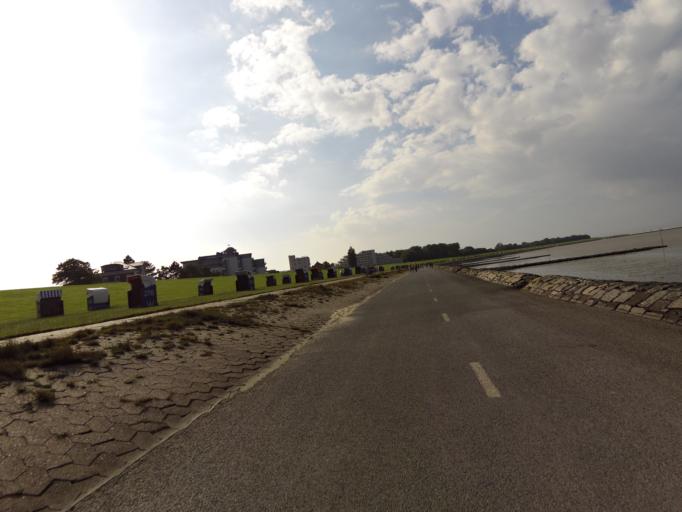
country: DE
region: Lower Saxony
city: Cuxhaven
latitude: 53.8791
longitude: 8.6881
